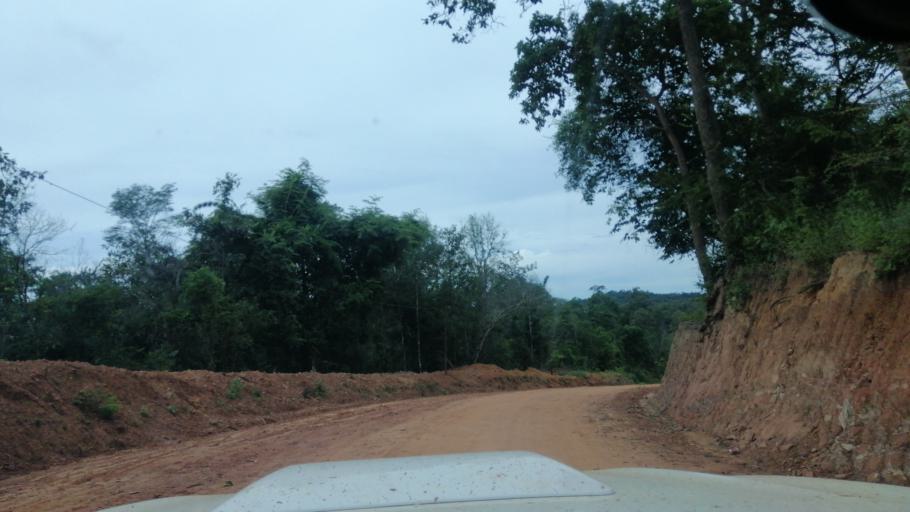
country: TH
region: Loei
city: Na Haeo
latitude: 17.5822
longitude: 101.1742
